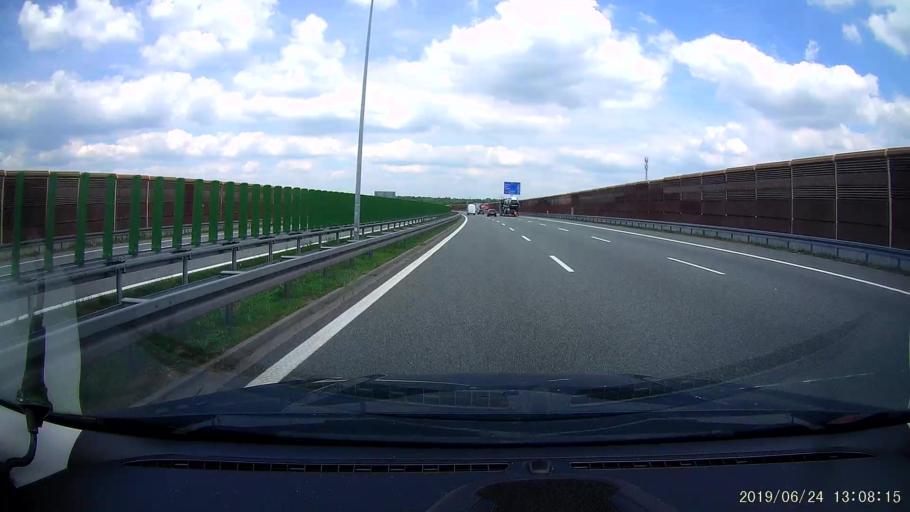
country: PL
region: Silesian Voivodeship
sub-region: Powiat rybnicki
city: Belk
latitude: 50.1705
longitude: 18.7154
